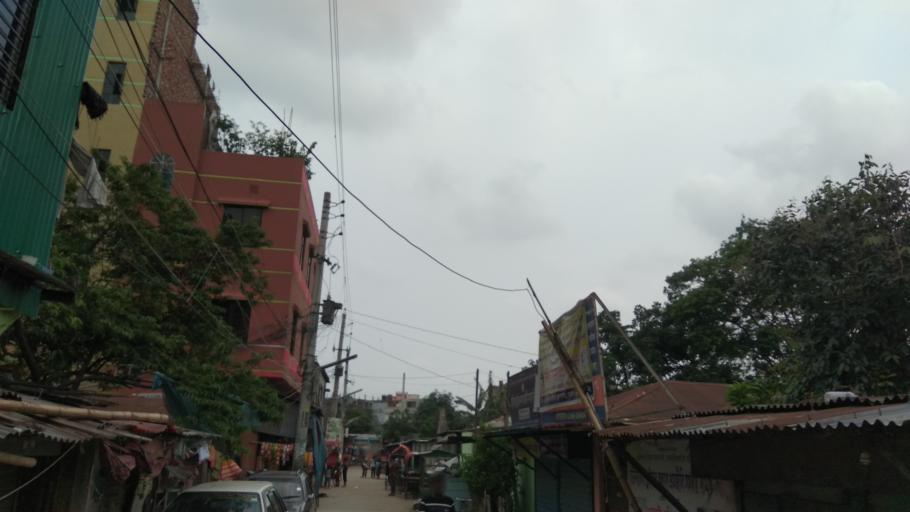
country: BD
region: Dhaka
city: Tungi
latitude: 23.8177
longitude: 90.3802
